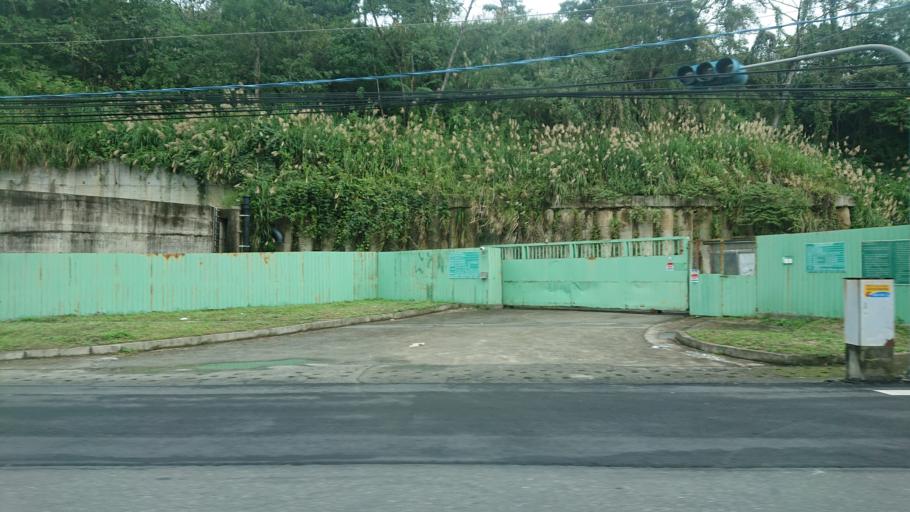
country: TW
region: Taiwan
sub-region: Taoyuan
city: Taoyuan
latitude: 24.9392
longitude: 121.3956
